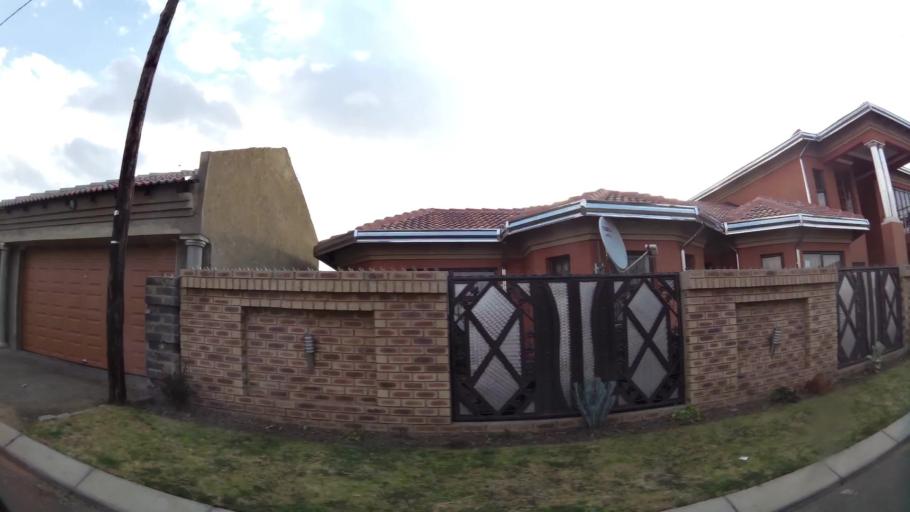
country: ZA
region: Gauteng
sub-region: Sedibeng District Municipality
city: Vanderbijlpark
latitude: -26.6094
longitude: 27.8150
